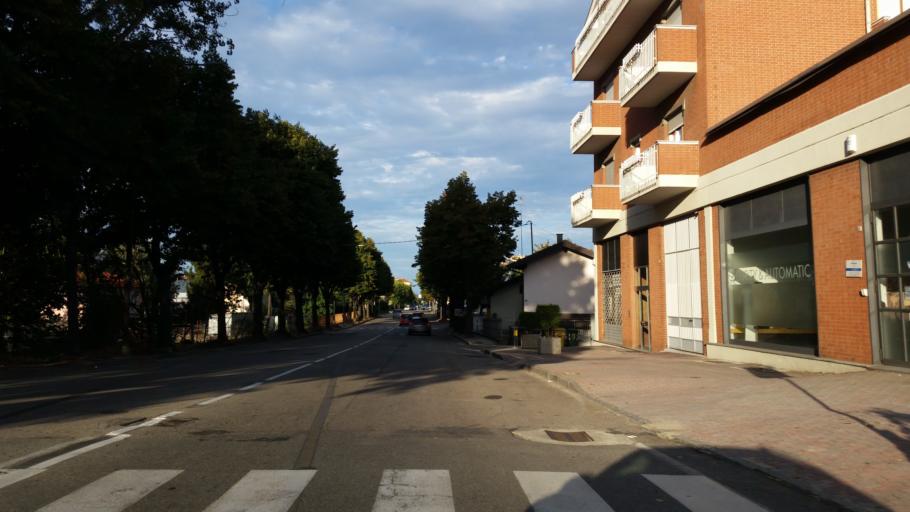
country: IT
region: Piedmont
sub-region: Provincia di Asti
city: Asti
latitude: 44.8914
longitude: 8.2031
